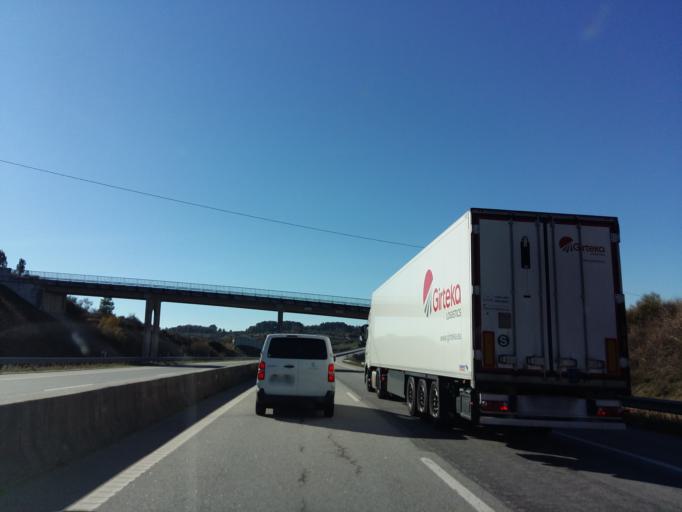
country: PT
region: Castelo Branco
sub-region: Covilha
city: Covilha
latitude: 40.2501
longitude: -7.4537
